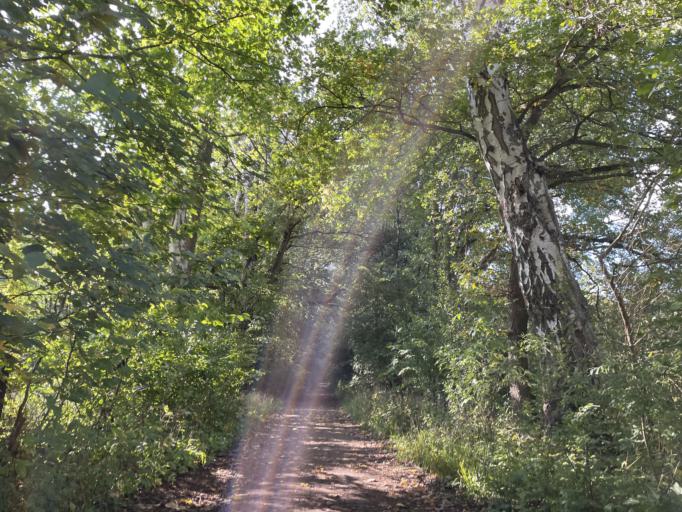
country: DE
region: Lower Saxony
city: Deutsch Evern
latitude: 53.2183
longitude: 10.4156
